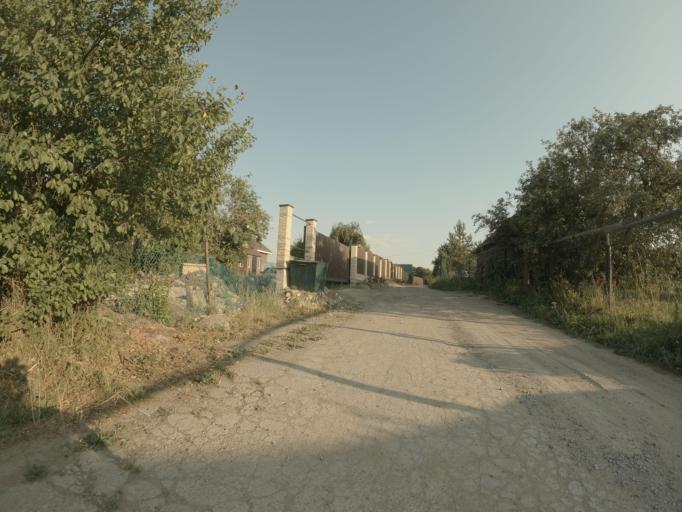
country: RU
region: Leningrad
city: Koltushi
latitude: 59.8904
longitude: 30.6979
